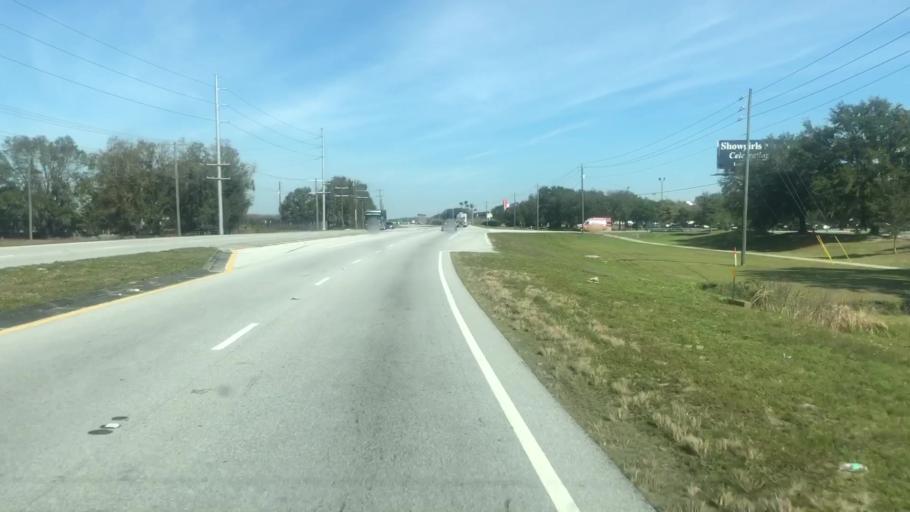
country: US
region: Florida
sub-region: Polk County
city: Winston
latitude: 28.0026
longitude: -82.0558
